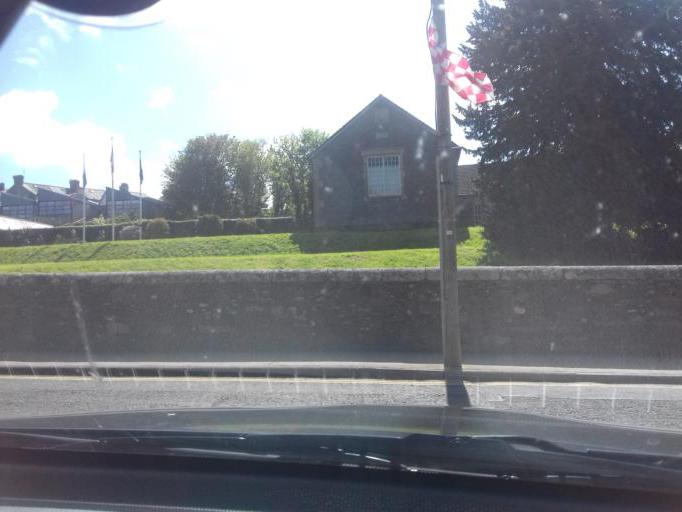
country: IE
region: Munster
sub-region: Waterford
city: Waterford
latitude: 52.2544
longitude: -7.1054
